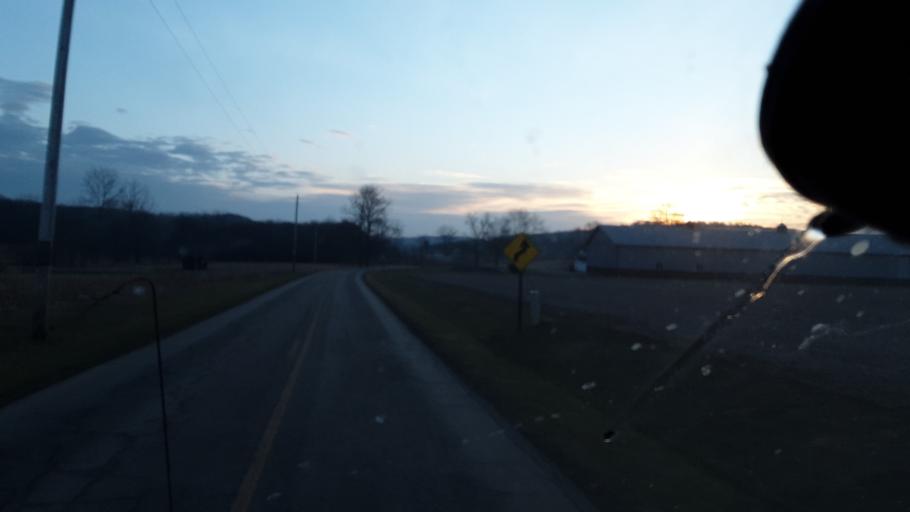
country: US
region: Ohio
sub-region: Knox County
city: Oak Hill
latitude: 40.4148
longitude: -82.2332
